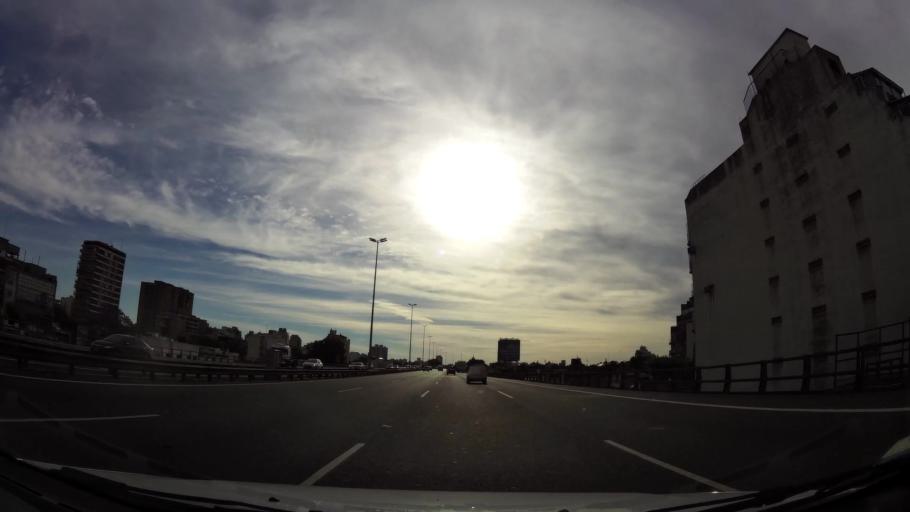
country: AR
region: Buenos Aires F.D.
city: Villa Santa Rita
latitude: -34.6355
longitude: -58.5000
